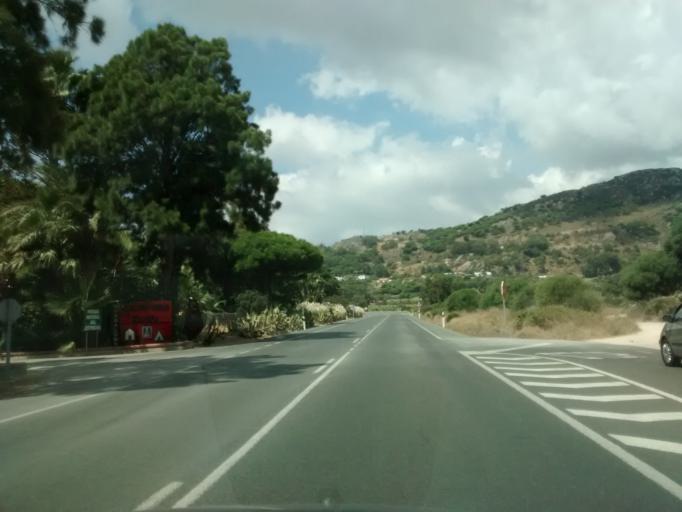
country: ES
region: Andalusia
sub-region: Provincia de Cadiz
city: Tarifa
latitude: 36.0547
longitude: -5.6493
